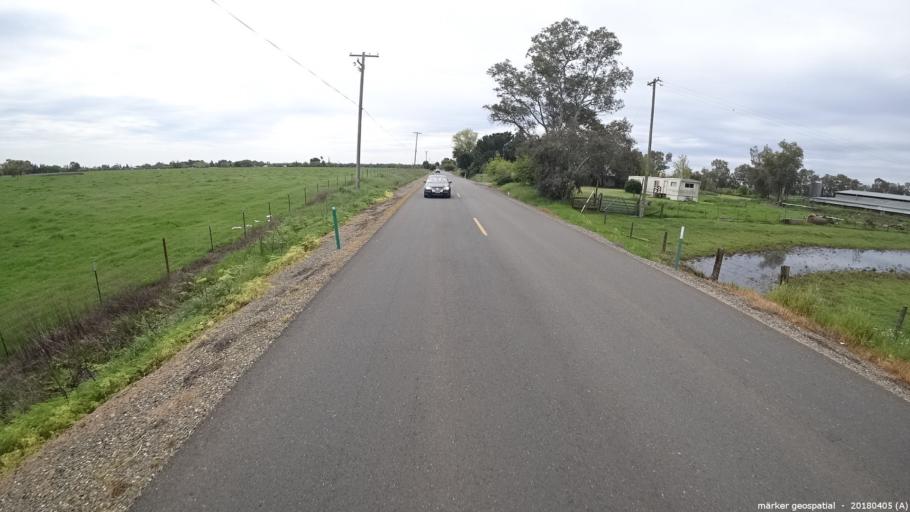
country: US
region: California
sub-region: Sacramento County
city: Galt
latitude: 38.2886
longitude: -121.3375
